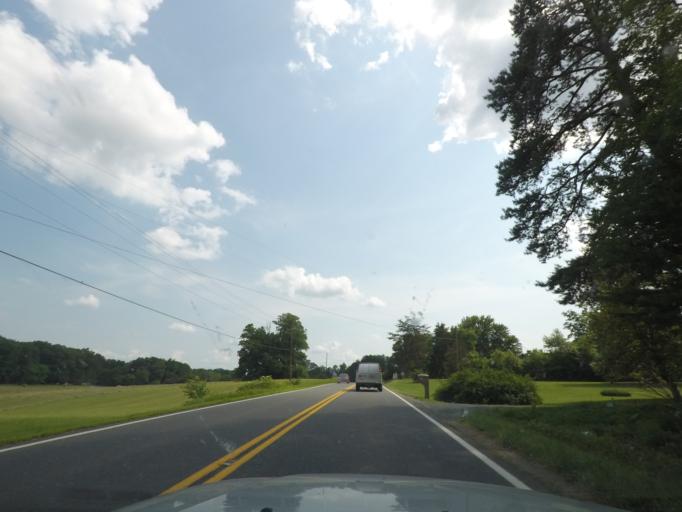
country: US
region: Virginia
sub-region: Fluvanna County
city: Palmyra
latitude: 37.9094
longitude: -78.2566
